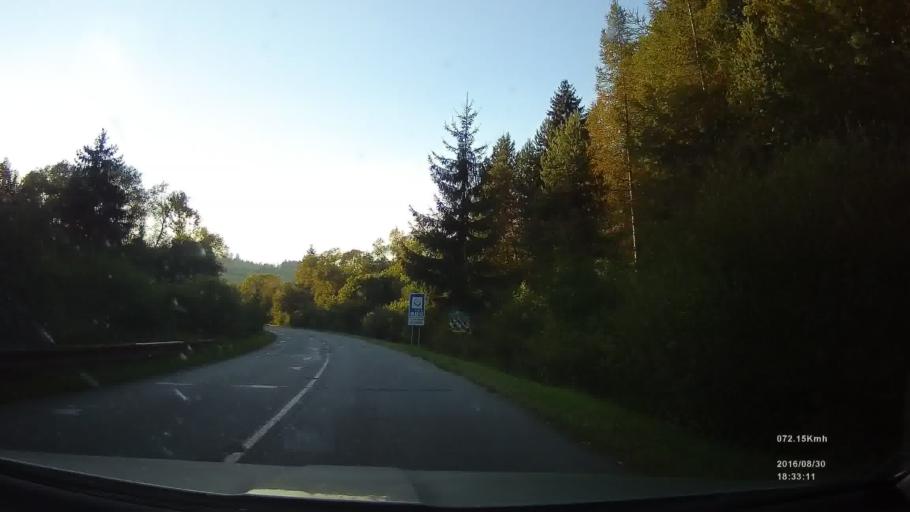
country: SK
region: Zilinsky
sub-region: Okres Liptovsky Mikulas
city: Liptovsky Mikulas
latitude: 49.1216
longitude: 19.4829
